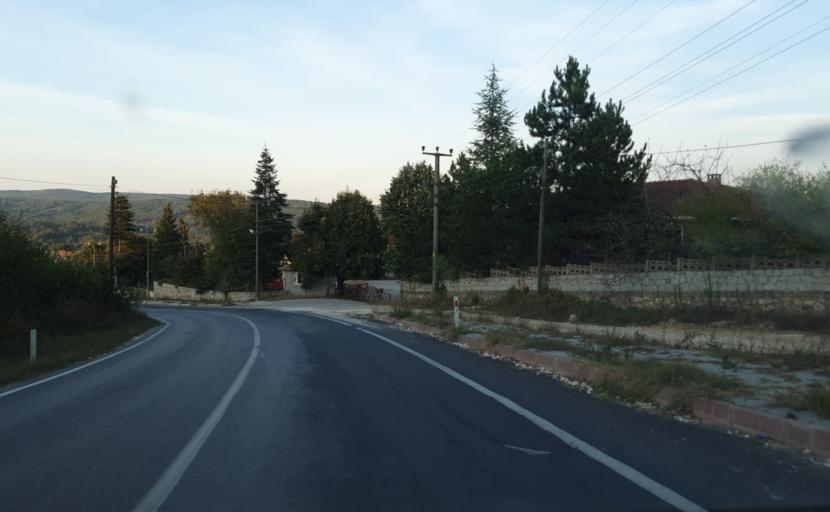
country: TR
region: Kirklareli
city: Sergen
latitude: 41.8251
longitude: 27.7769
